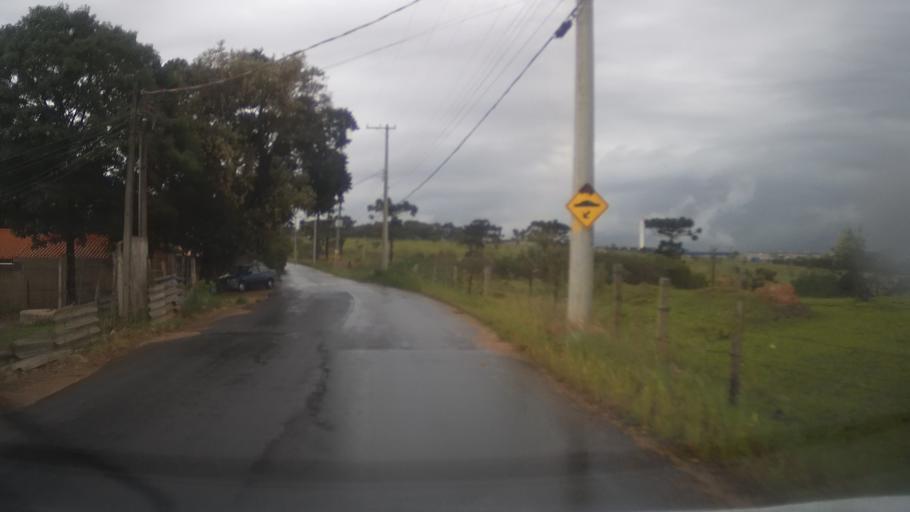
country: BR
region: Sao Paulo
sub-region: Itupeva
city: Itupeva
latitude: -23.1691
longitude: -47.0322
